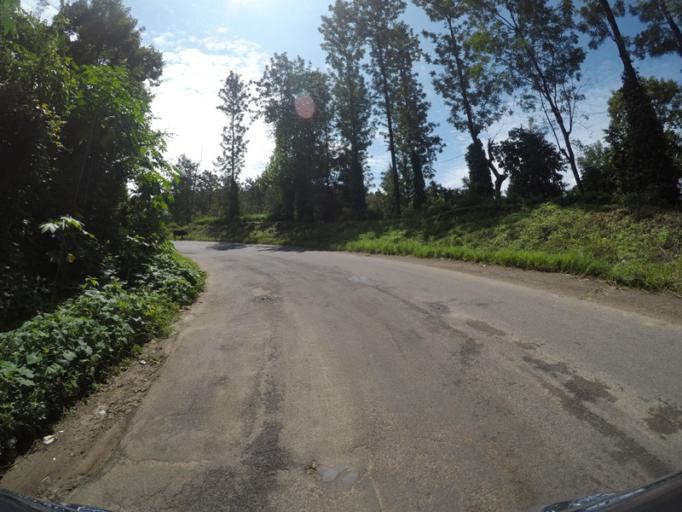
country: IN
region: Karnataka
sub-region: Kodagu
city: Suntikoppa
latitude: 12.5108
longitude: 75.8138
